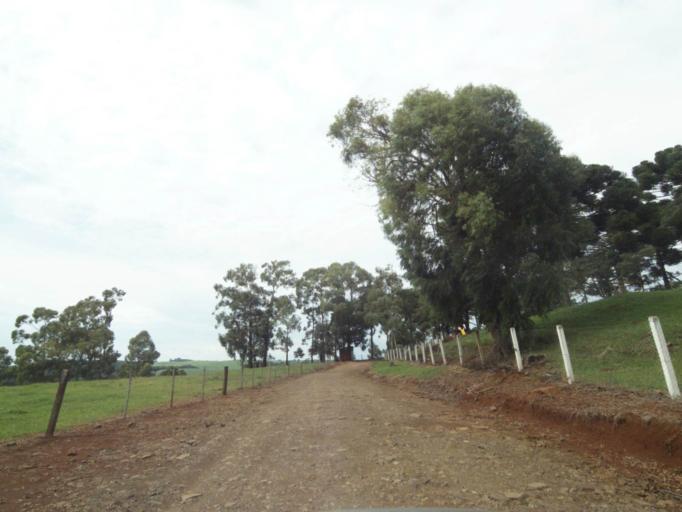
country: BR
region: Rio Grande do Sul
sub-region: Lagoa Vermelha
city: Lagoa Vermelha
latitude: -28.2262
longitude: -51.5164
